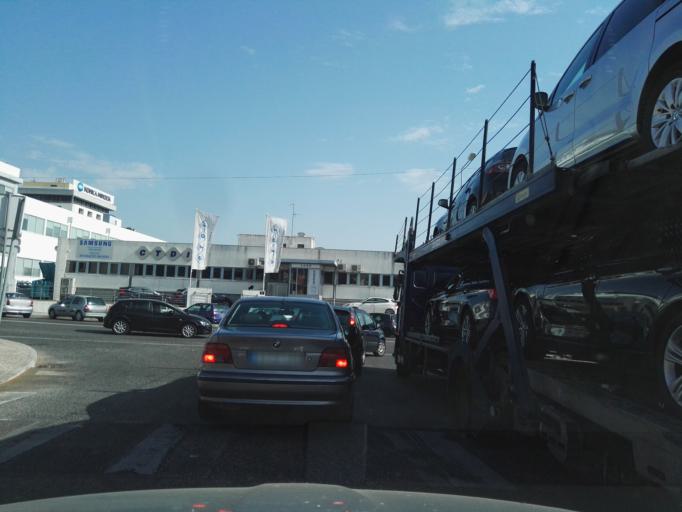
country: PT
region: Lisbon
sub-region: Loures
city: Sacavem
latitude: 38.7858
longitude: -9.1243
